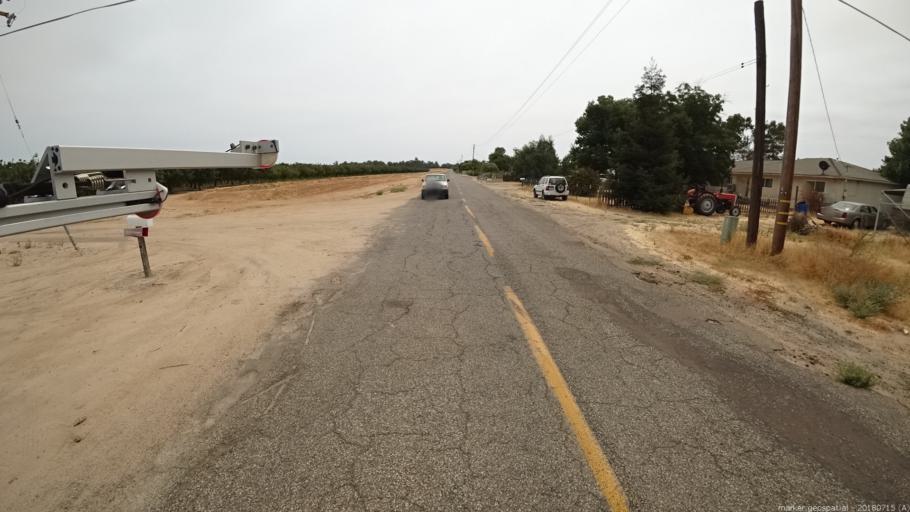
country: US
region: California
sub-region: Madera County
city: Madera Acres
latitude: 37.0255
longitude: -120.0880
